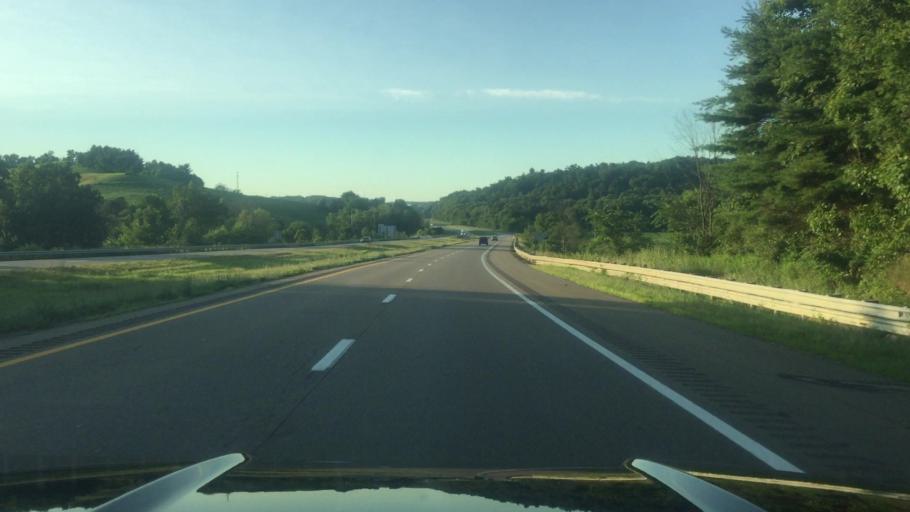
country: US
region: Ohio
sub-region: Tuscarawas County
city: Newcomerstown
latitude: 40.3183
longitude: -81.5697
